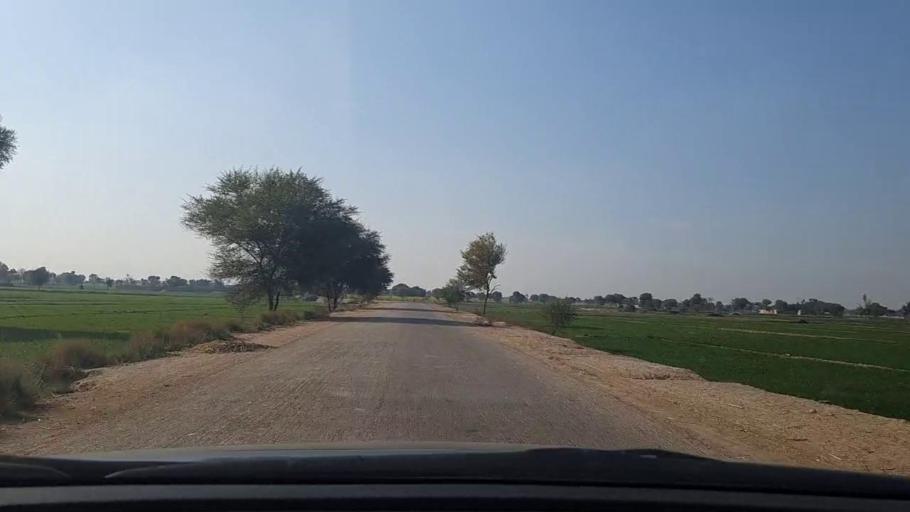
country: PK
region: Sindh
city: Daulatpur
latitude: 26.3188
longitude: 68.0526
